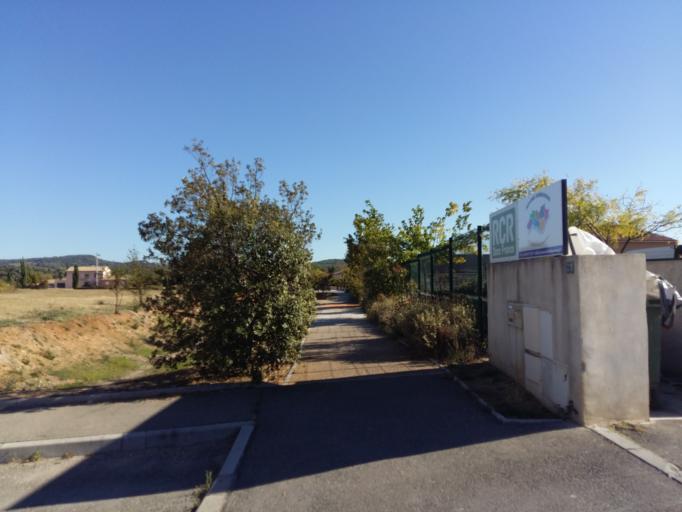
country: FR
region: Provence-Alpes-Cote d'Azur
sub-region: Departement du Vaucluse
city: Pertuis
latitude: 43.7232
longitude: 5.5381
